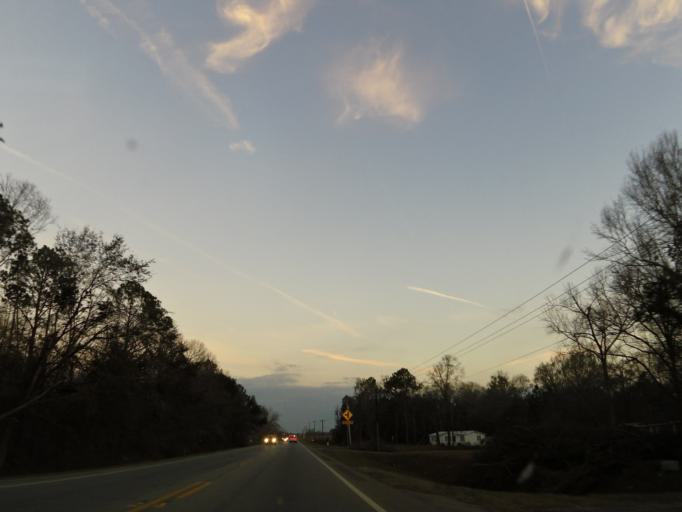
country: US
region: Georgia
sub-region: Dougherty County
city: Putney
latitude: 31.5348
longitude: -84.0968
